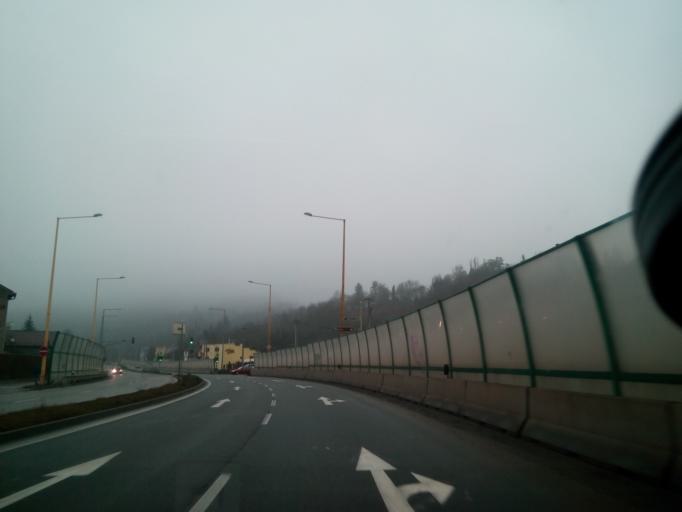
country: SK
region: Presovsky
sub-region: Okres Presov
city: Presov
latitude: 48.9905
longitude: 21.2292
